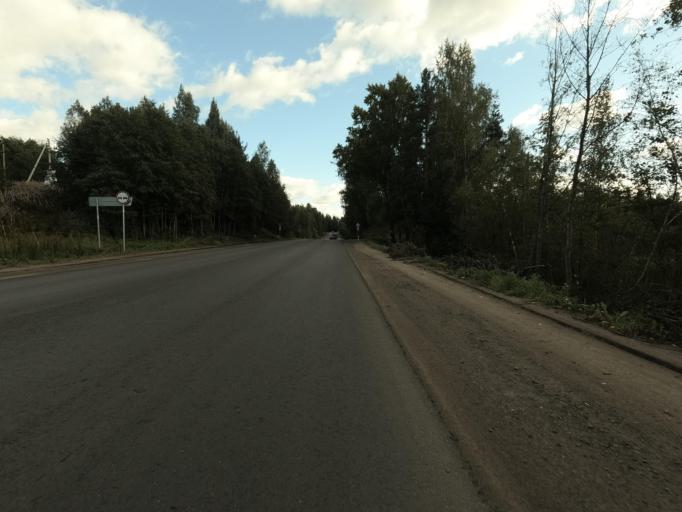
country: RU
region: Leningrad
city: Koltushi
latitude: 59.9695
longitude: 30.6549
